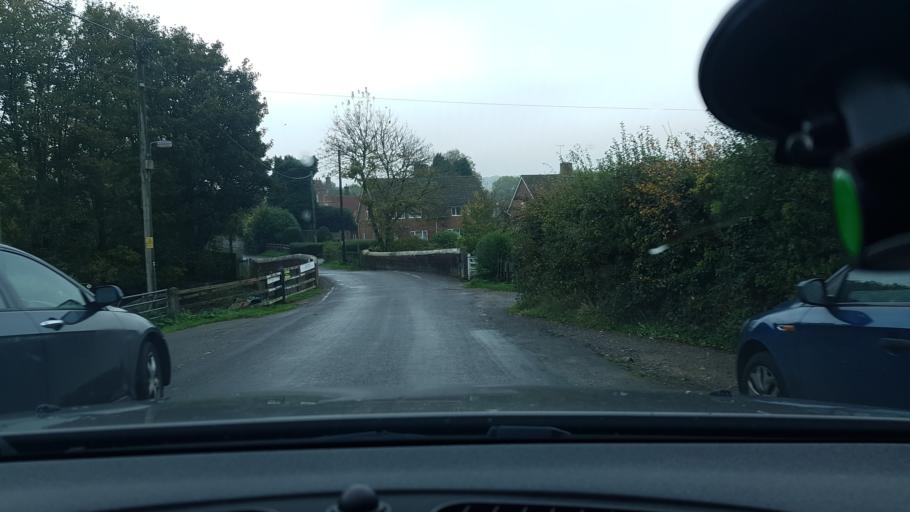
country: GB
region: England
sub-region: Wiltshire
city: Burbage
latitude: 51.3647
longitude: -1.7161
